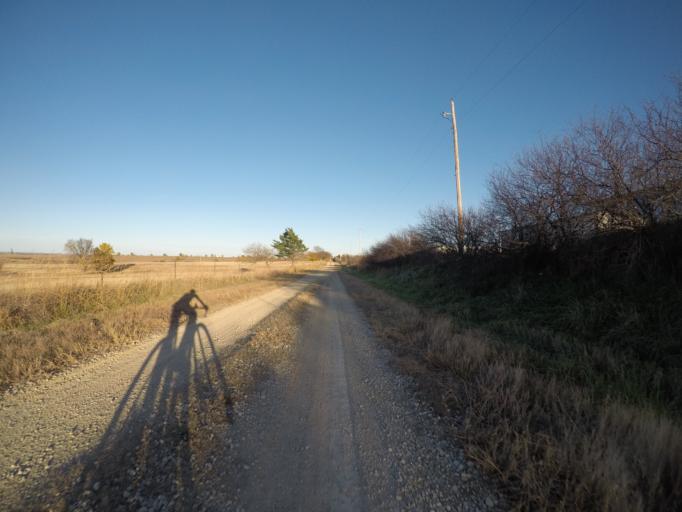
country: US
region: Kansas
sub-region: Riley County
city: Manhattan
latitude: 39.2544
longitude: -96.6657
